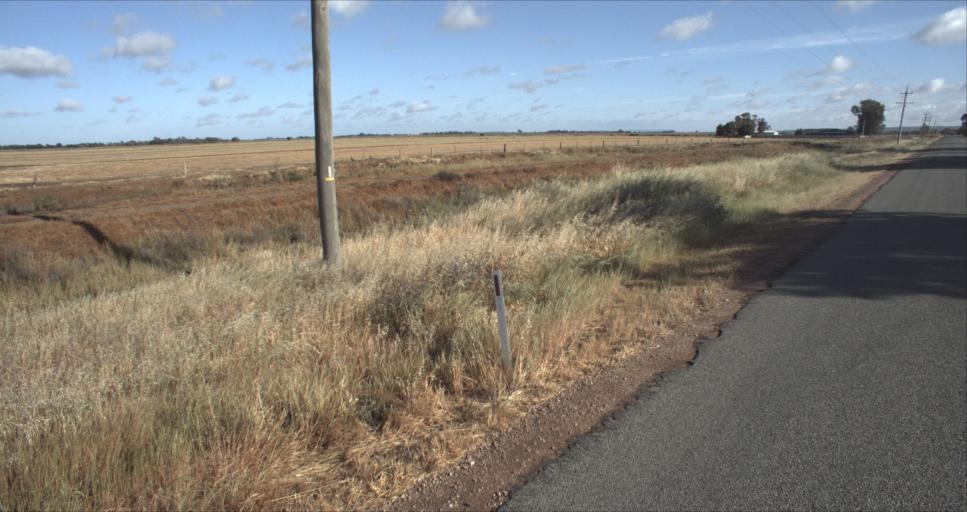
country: AU
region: New South Wales
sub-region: Leeton
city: Leeton
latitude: -34.5206
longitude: 146.3906
